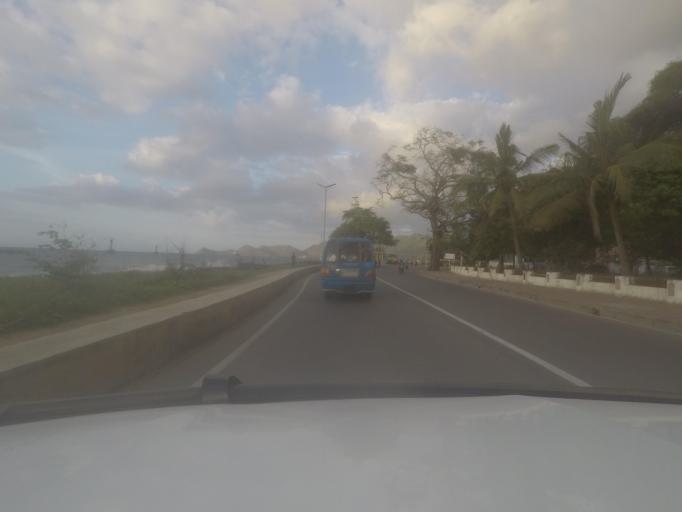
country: TL
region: Dili
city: Dili
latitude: -8.5485
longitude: 125.5678
